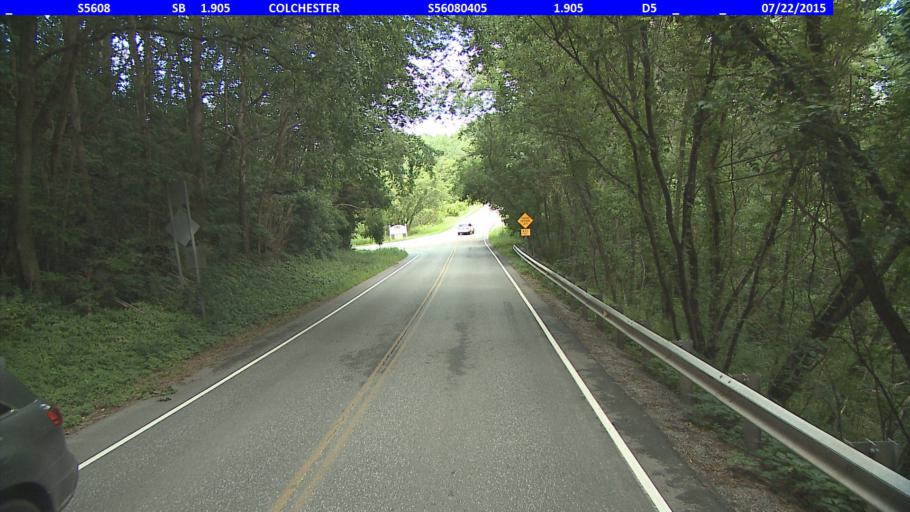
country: US
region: Vermont
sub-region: Chittenden County
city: Winooski
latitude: 44.5246
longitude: -73.2054
